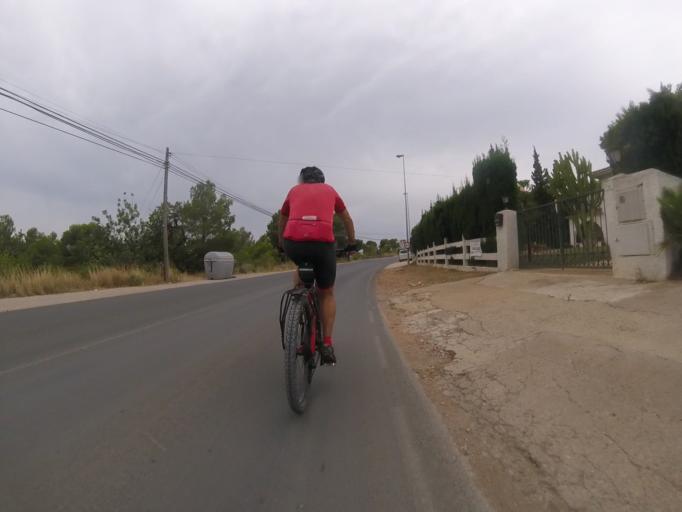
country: ES
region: Valencia
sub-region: Provincia de Castello
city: Alcoceber
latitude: 40.2507
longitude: 0.2772
